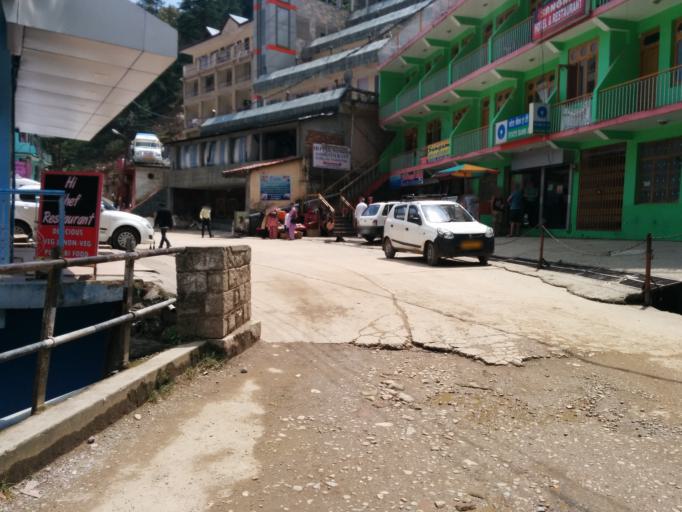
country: IN
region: Himachal Pradesh
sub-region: Kangra
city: Dharmsala
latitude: 32.2434
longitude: 76.3321
